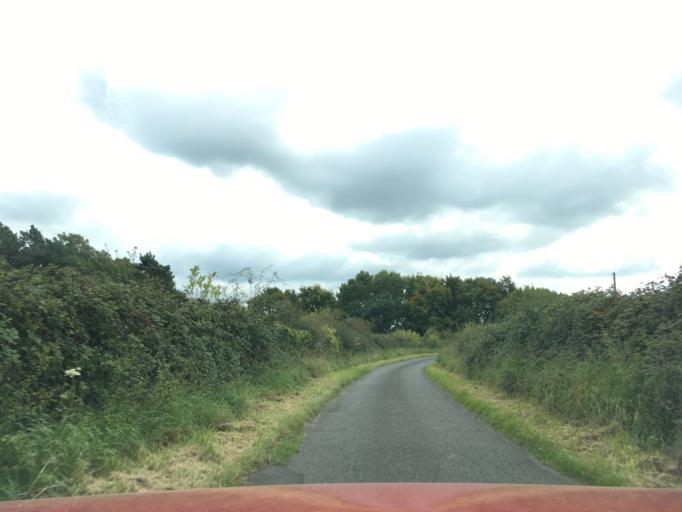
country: GB
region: England
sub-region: South Gloucestershire
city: Charfield
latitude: 51.6238
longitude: -2.4307
